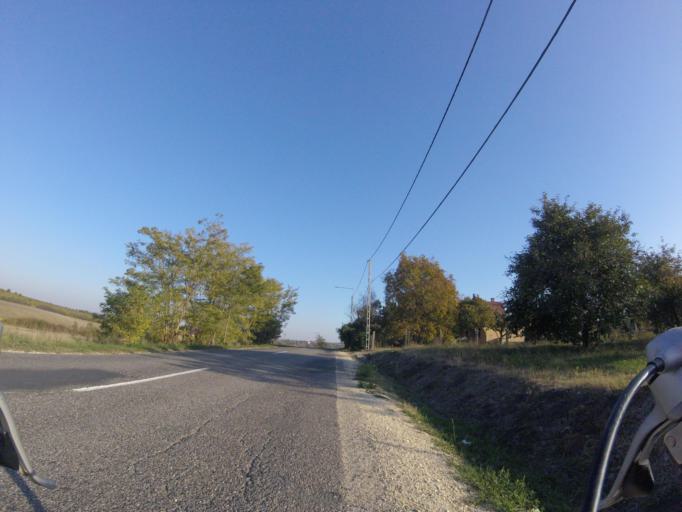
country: HU
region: Fejer
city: Etyek
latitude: 47.4528
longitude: 18.7358
